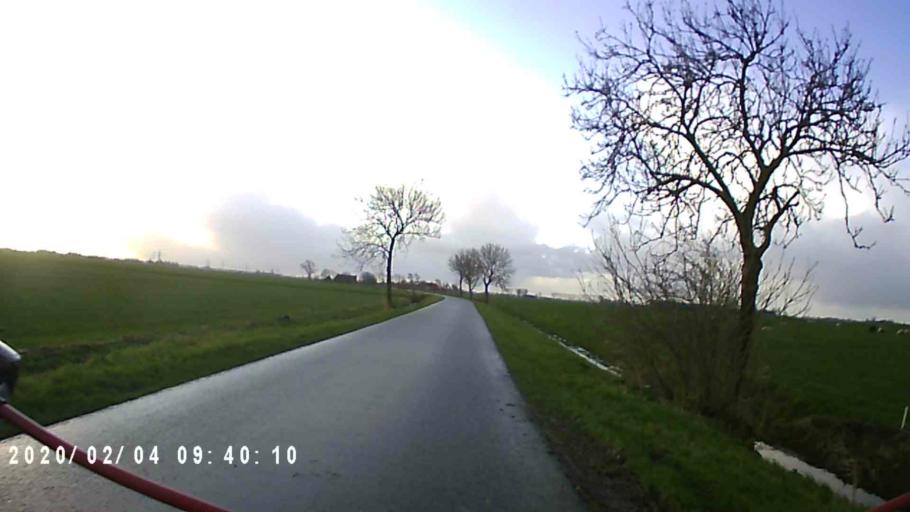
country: NL
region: Groningen
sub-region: Gemeente Zuidhorn
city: Aduard
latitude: 53.3002
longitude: 6.4692
